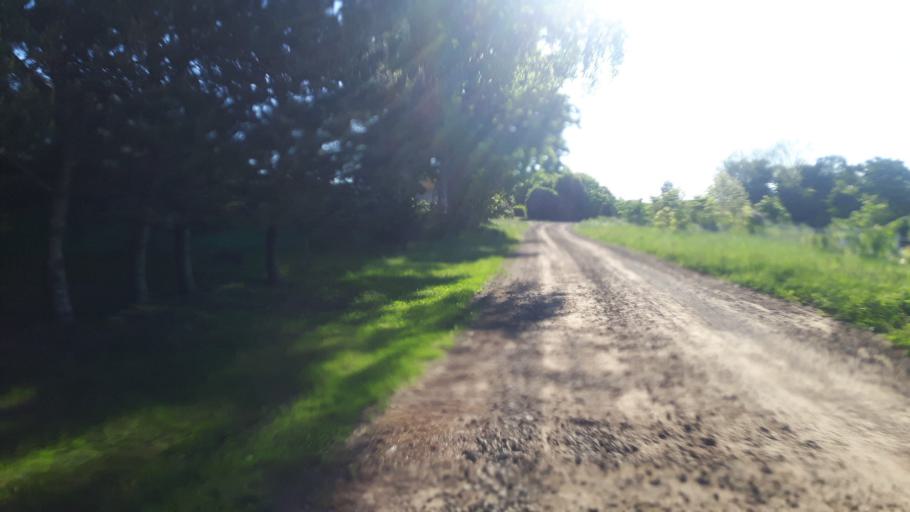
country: EE
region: Ida-Virumaa
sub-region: Puessi linn
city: Pussi
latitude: 59.4259
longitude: 27.0926
